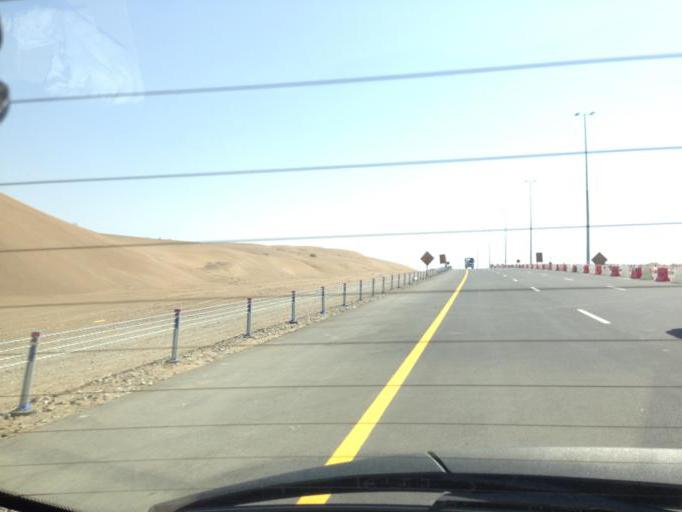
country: OM
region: Al Batinah
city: Bayt al `Awabi
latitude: 23.5183
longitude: 57.6290
